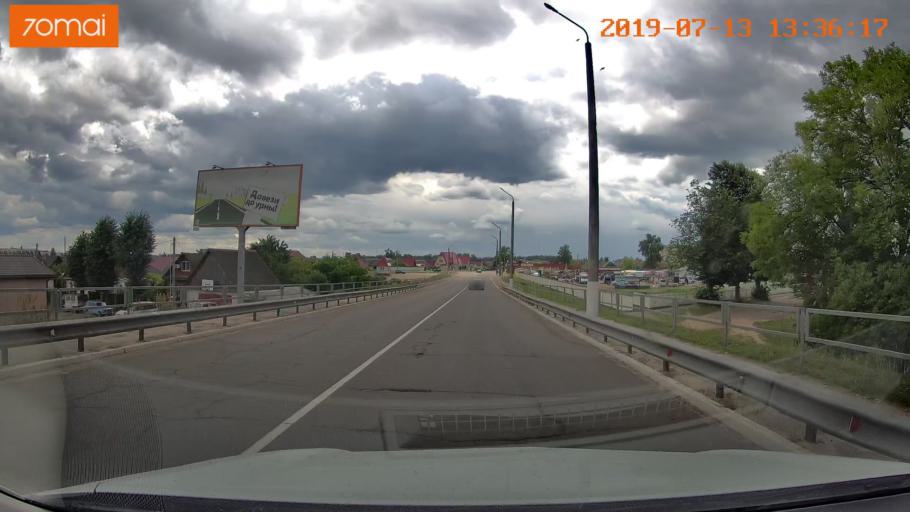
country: BY
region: Mogilev
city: Asipovichy
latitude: 53.3031
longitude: 28.6232
